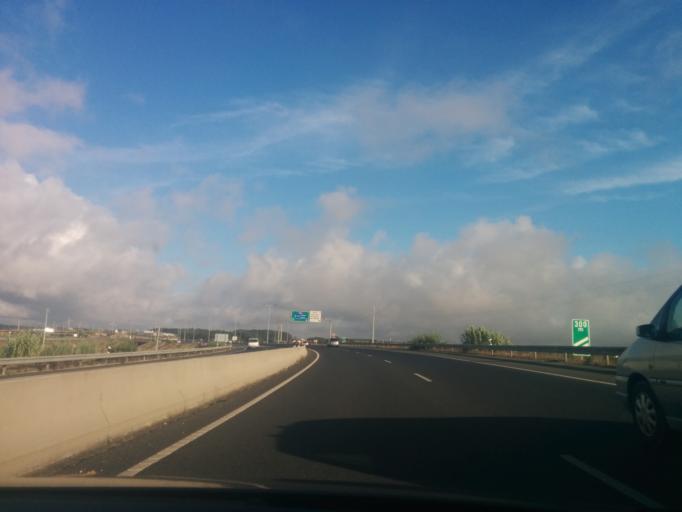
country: PT
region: Leiria
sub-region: Peniche
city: Atouguia da Baleia
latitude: 39.3330
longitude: -9.3345
